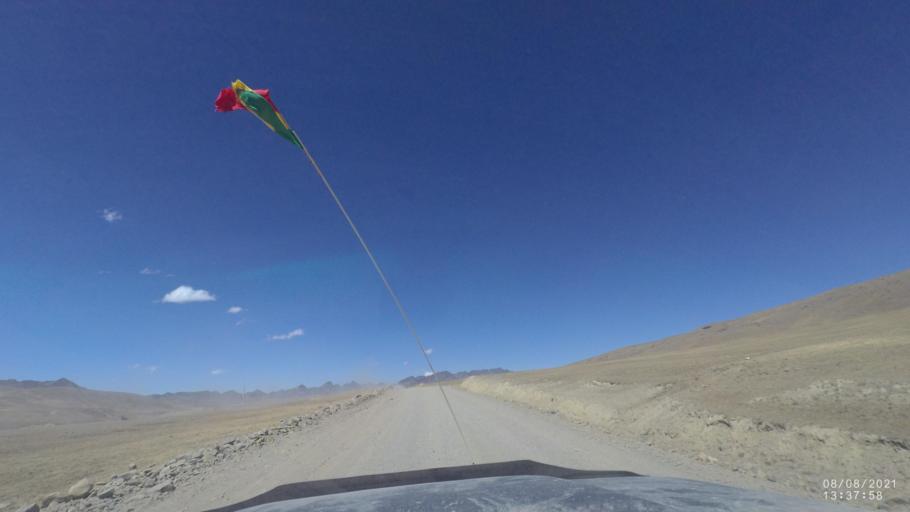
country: BO
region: Cochabamba
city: Colchani
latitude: -17.0836
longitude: -66.4918
